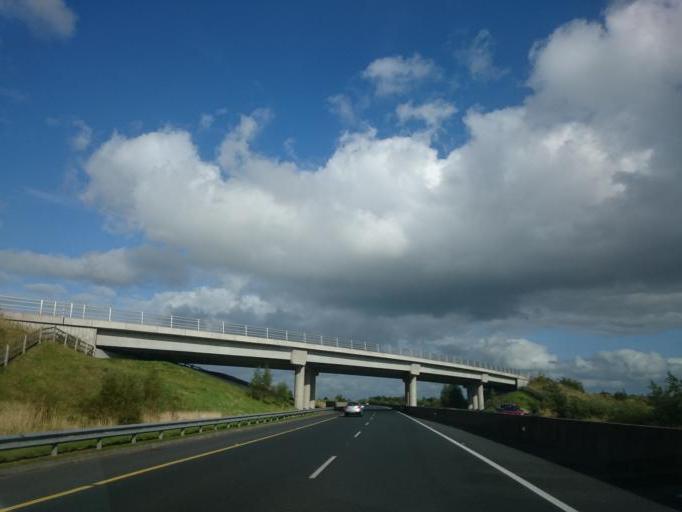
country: IE
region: Connaught
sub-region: County Galway
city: Athenry
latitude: 53.2764
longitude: -8.7197
